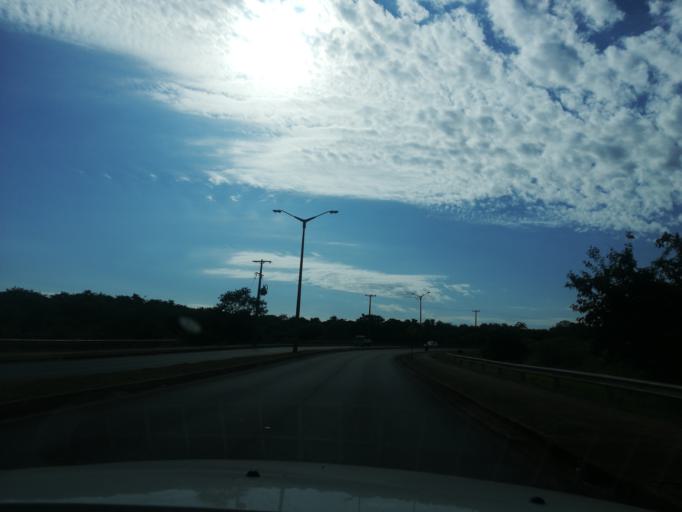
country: PY
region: Itapua
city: Encarnacion
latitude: -27.3469
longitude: -55.8504
